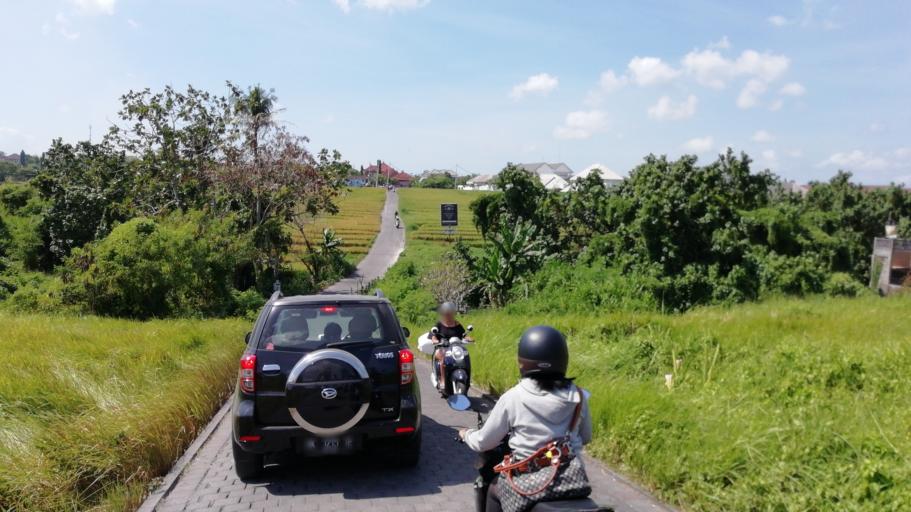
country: ID
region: Bali
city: Banjar Kerobokan
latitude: -8.6530
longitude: 115.1383
